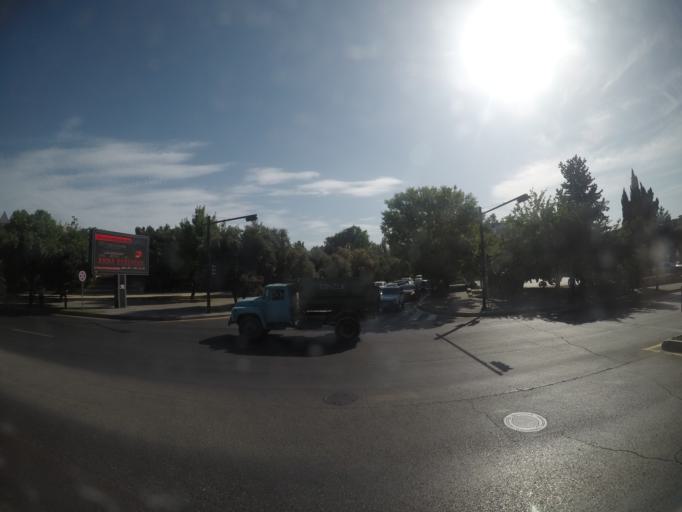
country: AZ
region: Baki
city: Badamdar
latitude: 40.3893
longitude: 49.8256
